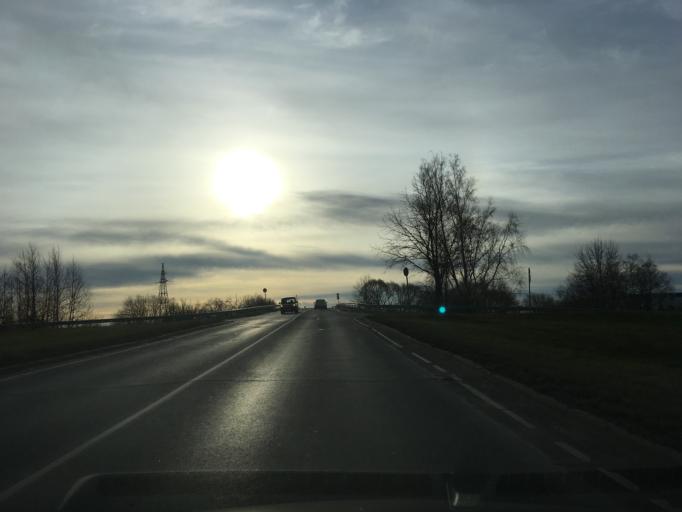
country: EE
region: Ida-Virumaa
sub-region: Narva linn
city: Narva
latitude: 59.3736
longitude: 28.1547
